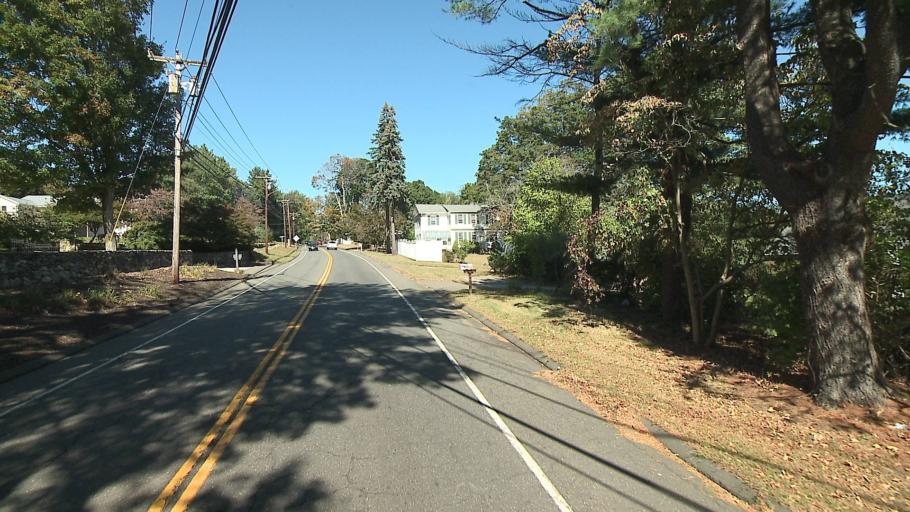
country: US
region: Connecticut
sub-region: New Haven County
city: Orange
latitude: 41.2925
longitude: -73.0410
